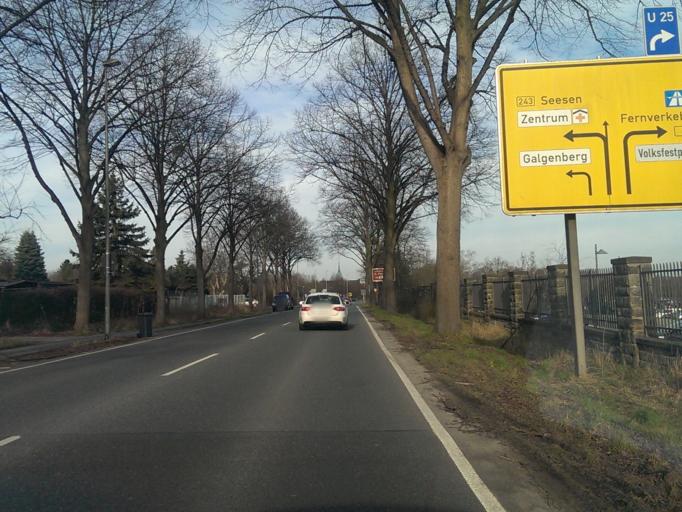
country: DE
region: Lower Saxony
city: Hildesheim
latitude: 52.1497
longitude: 9.9765
